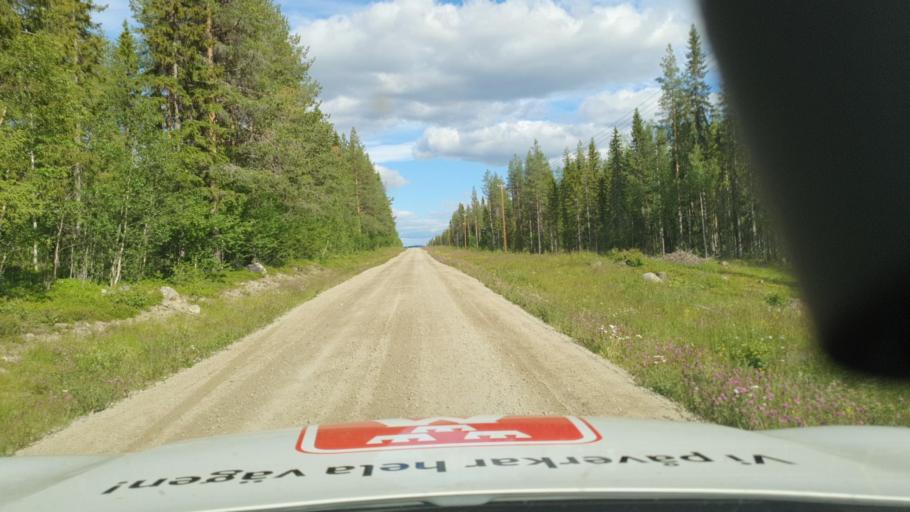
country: SE
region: Vaesterbotten
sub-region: Lycksele Kommun
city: Lycksele
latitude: 64.2960
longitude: 18.2451
